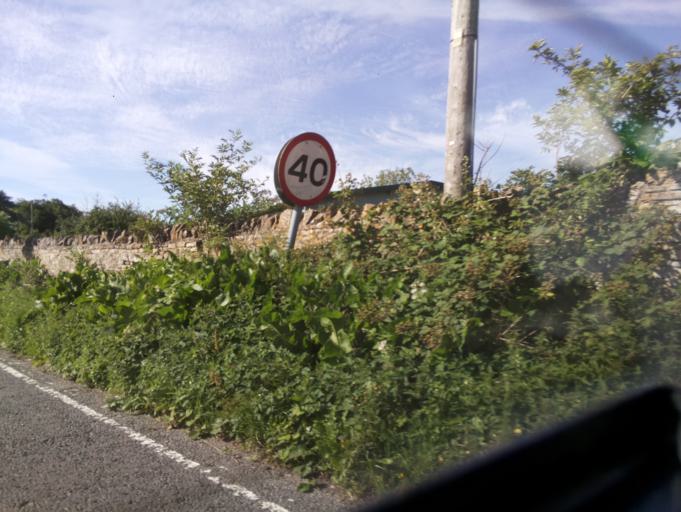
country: GB
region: England
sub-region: South Gloucestershire
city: Pucklechurch
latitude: 51.4518
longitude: -2.4179
